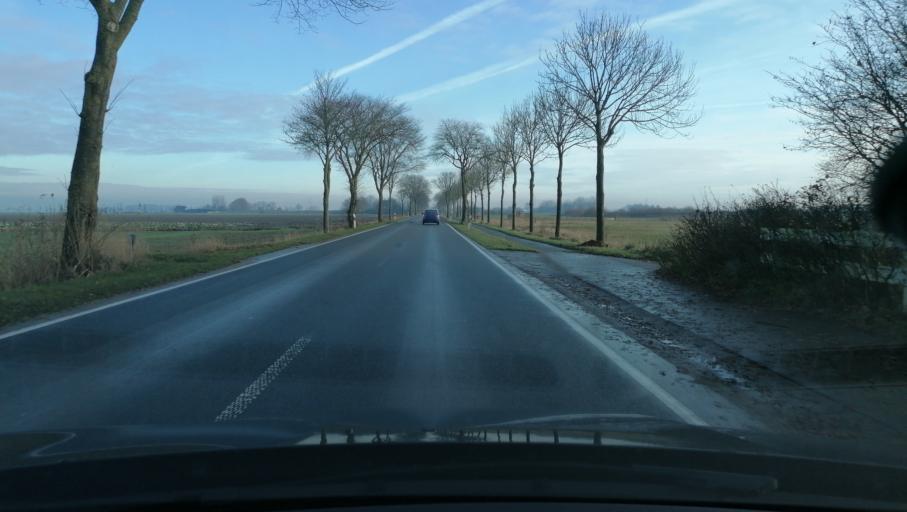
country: DE
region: Schleswig-Holstein
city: Wohrden
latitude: 54.1214
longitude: 8.9995
